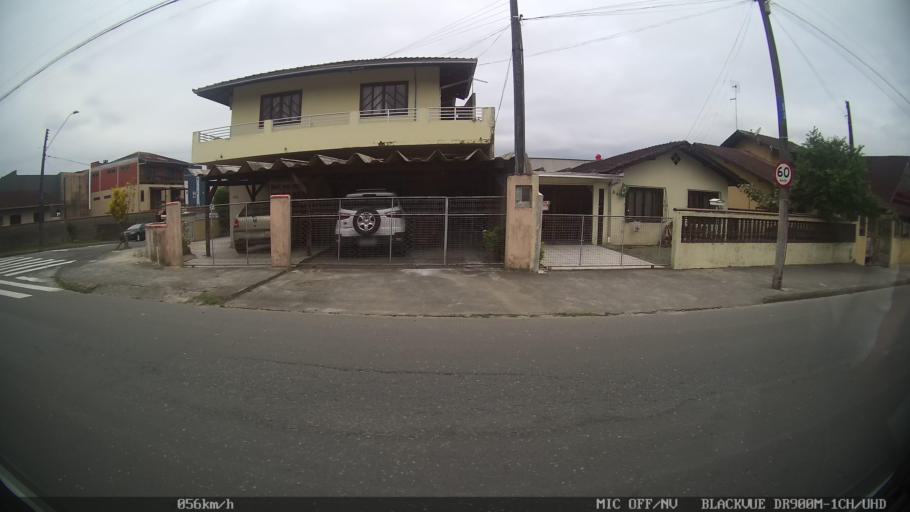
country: BR
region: Santa Catarina
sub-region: Joinville
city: Joinville
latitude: -26.2770
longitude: -48.8752
